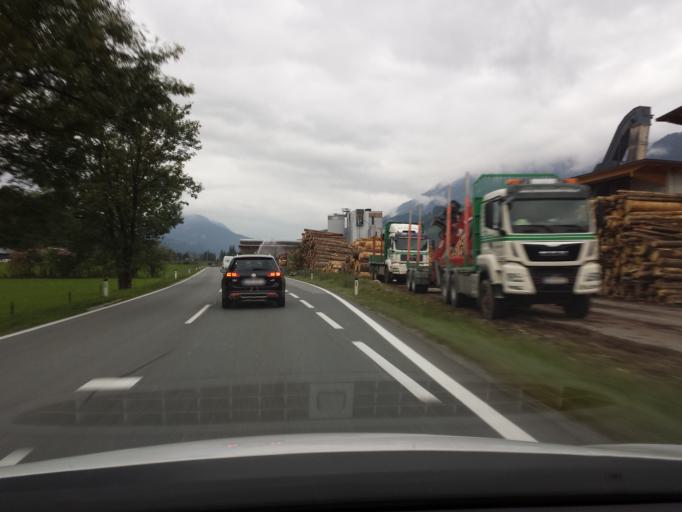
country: AT
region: Salzburg
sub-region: Politischer Bezirk Zell am See
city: Saalfelden am Steinernen Meer
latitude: 47.4403
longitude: 12.8150
